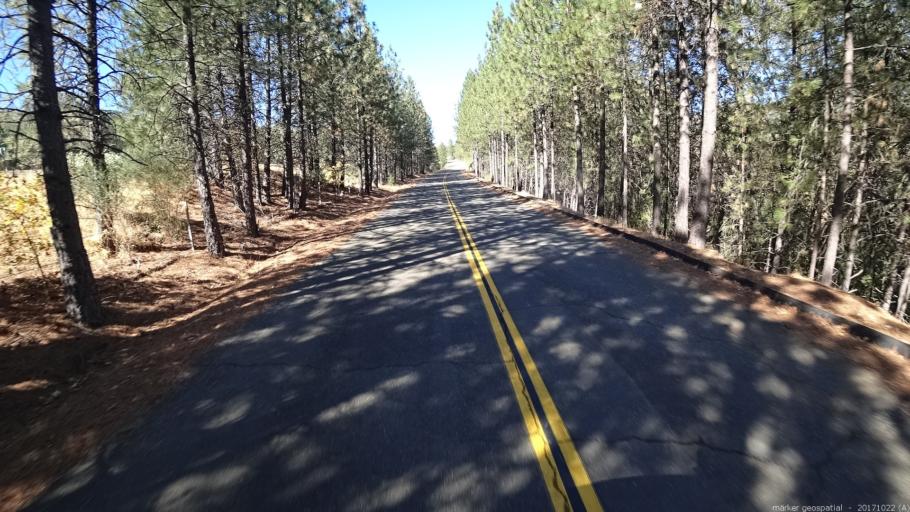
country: US
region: California
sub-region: Shasta County
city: Central Valley (historical)
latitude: 40.9194
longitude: -122.3979
